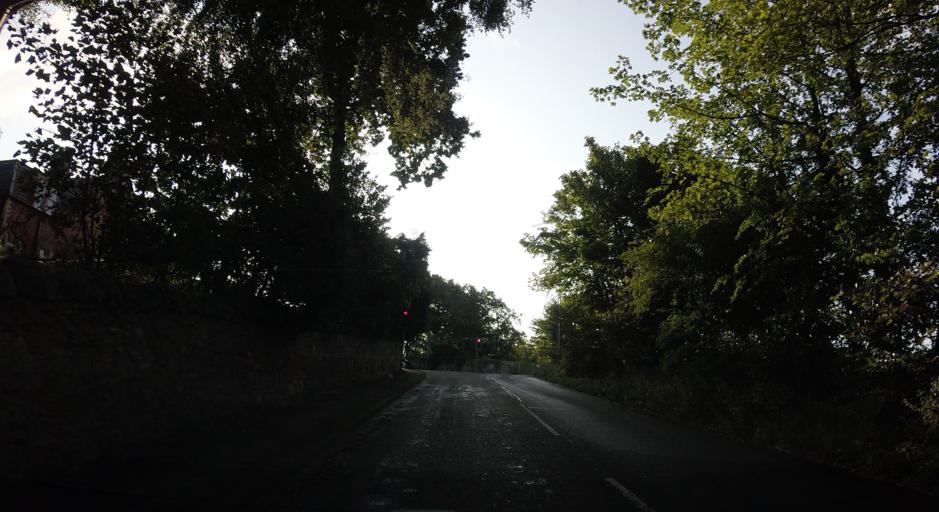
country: GB
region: Scotland
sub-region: East Lothian
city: Musselburgh
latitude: 55.9094
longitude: -3.0135
